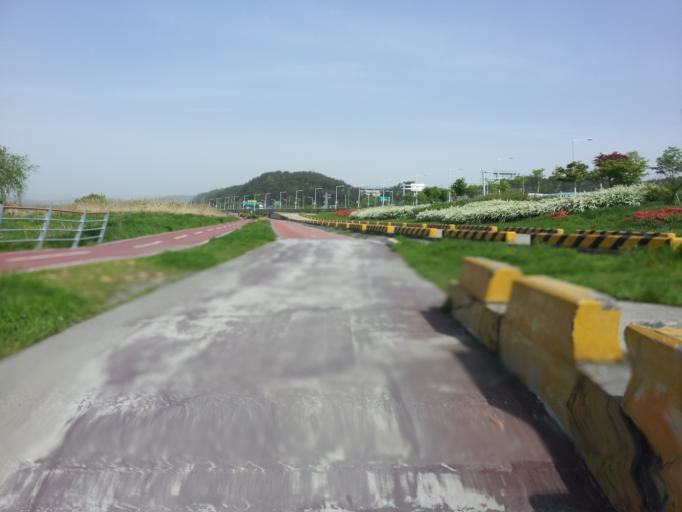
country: KR
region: Daejeon
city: Daejeon
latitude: 36.3574
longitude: 127.4044
